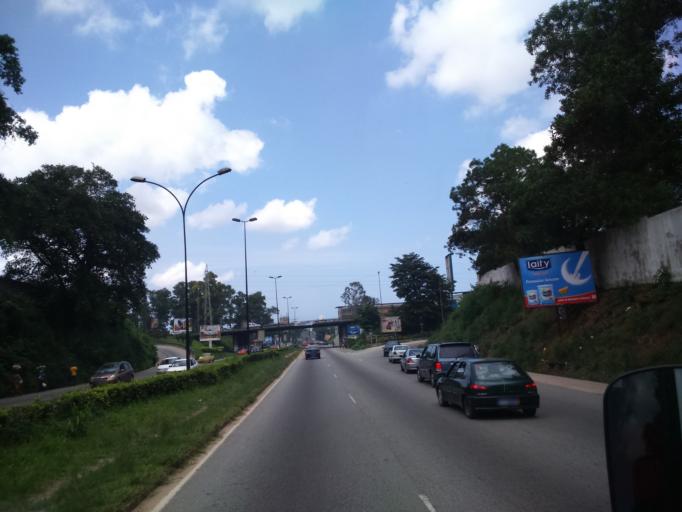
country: CI
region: Lagunes
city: Abidjan
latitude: 5.3559
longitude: -4.0016
